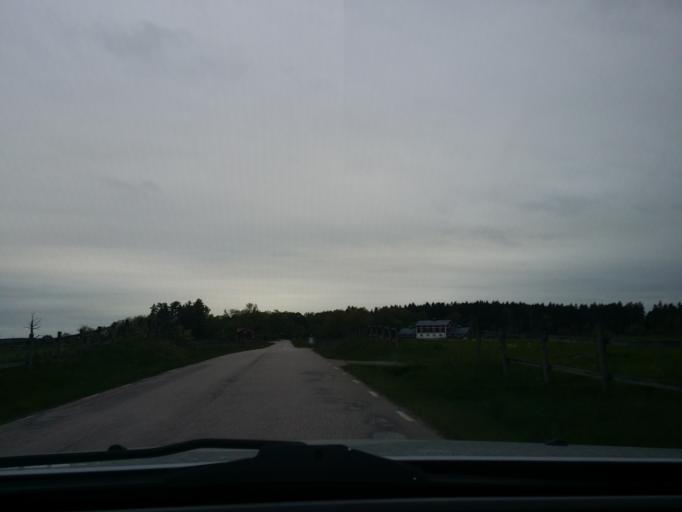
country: SE
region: Vaestmanland
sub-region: Hallstahammars Kommun
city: Kolback
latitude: 59.5323
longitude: 16.2936
